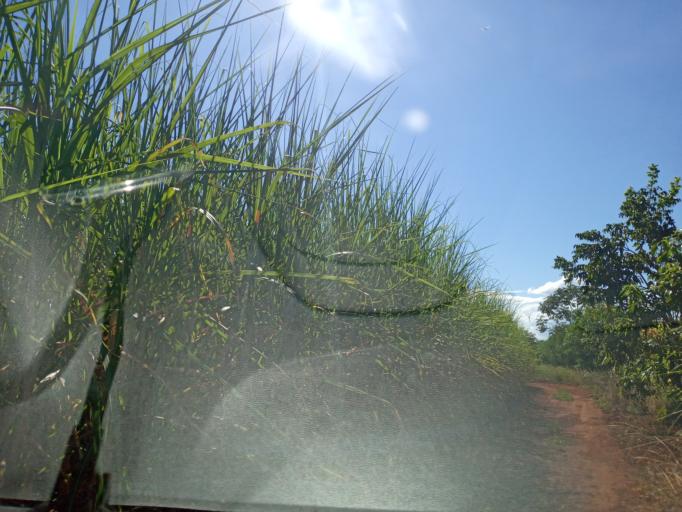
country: BR
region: Goias
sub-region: Itumbiara
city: Itumbiara
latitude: -18.4335
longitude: -49.0898
